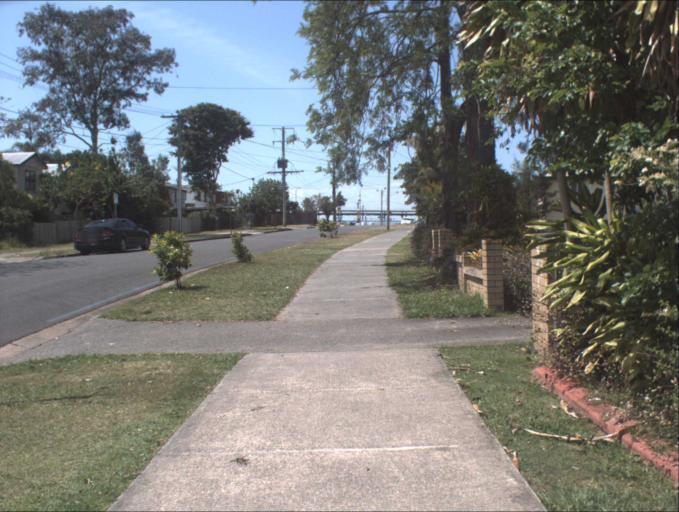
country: AU
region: Queensland
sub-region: Logan
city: Logan City
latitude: -27.6398
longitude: 153.1026
